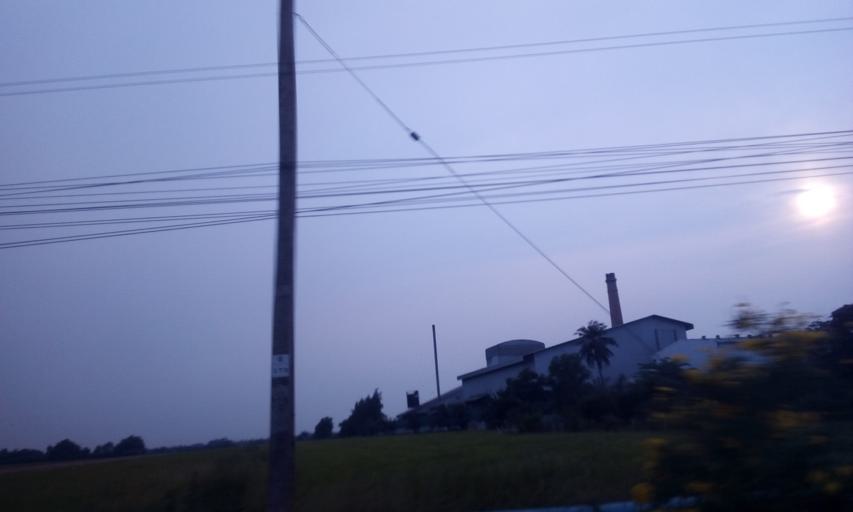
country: TH
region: Bangkok
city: Nong Chok
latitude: 13.8312
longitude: 100.9125
